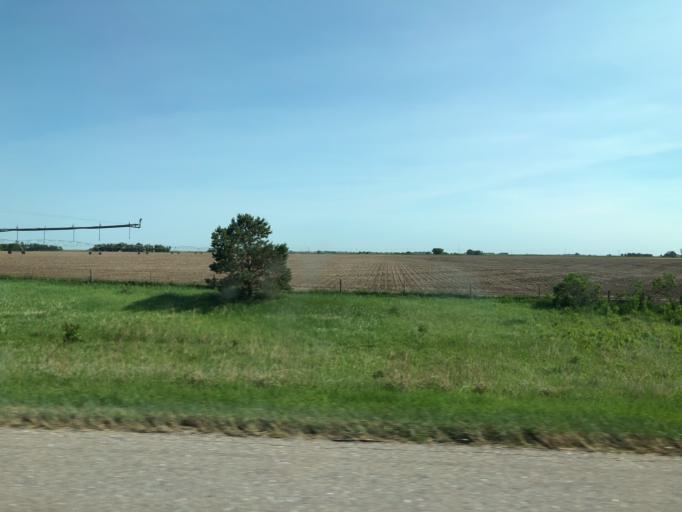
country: US
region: Nebraska
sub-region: Seward County
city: Seward
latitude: 40.8222
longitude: -97.1660
